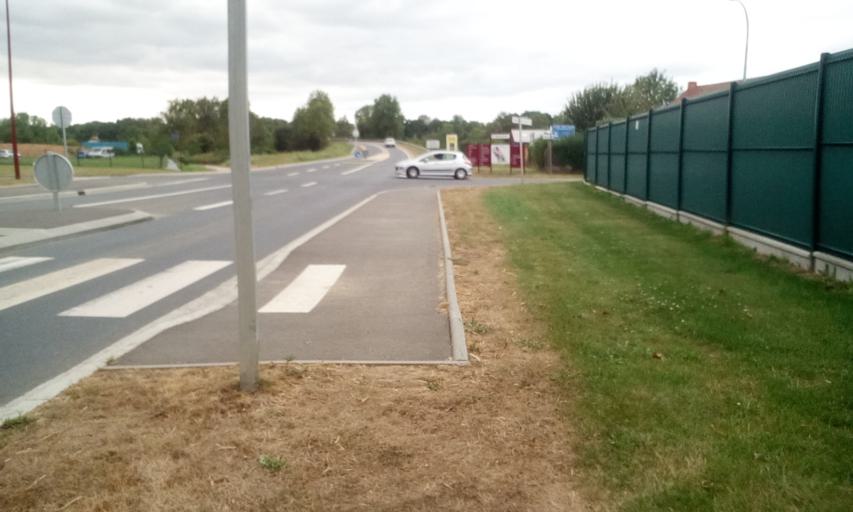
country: FR
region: Lower Normandy
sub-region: Departement du Calvados
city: Troarn
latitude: 49.1868
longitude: -0.1894
